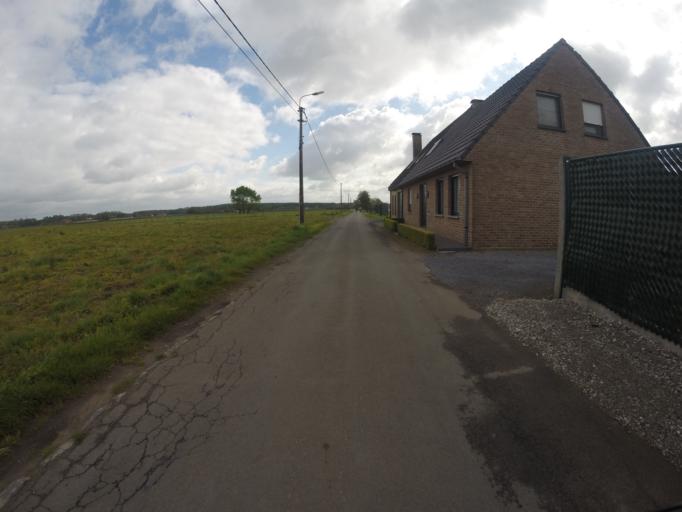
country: BE
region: Flanders
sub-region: Provincie West-Vlaanderen
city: Ruiselede
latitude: 51.0549
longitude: 3.3928
